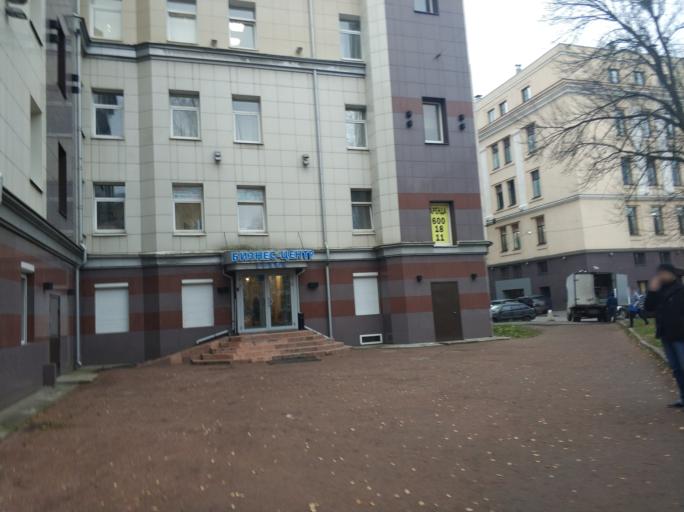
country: RU
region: Leningrad
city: Sampsonievskiy
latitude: 59.9708
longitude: 30.3404
